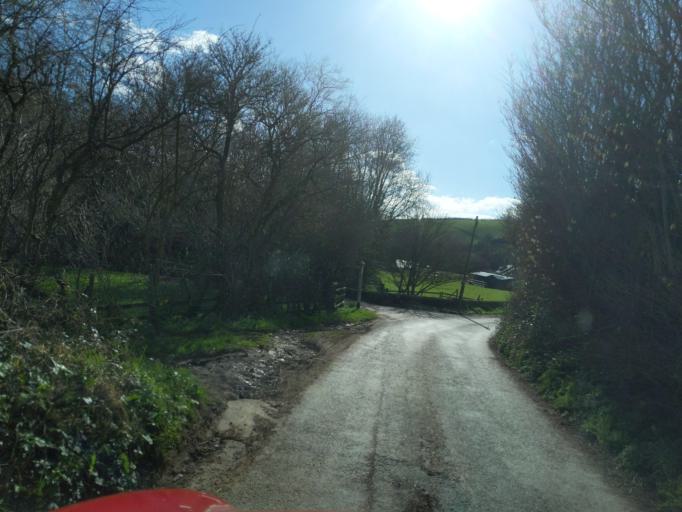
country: GB
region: England
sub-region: Devon
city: Kingsbridge
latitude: 50.2865
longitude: -3.7553
